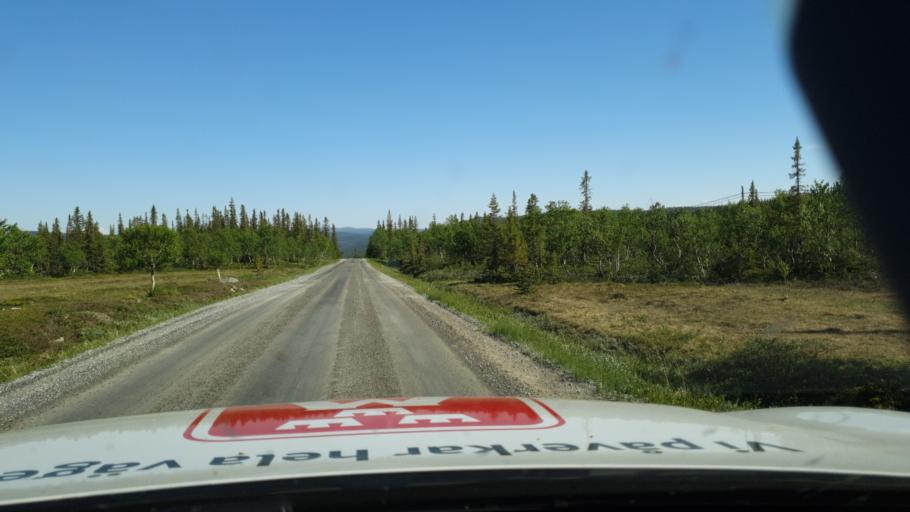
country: SE
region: Jaemtland
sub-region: Are Kommun
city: Are
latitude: 62.8744
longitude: 12.7382
